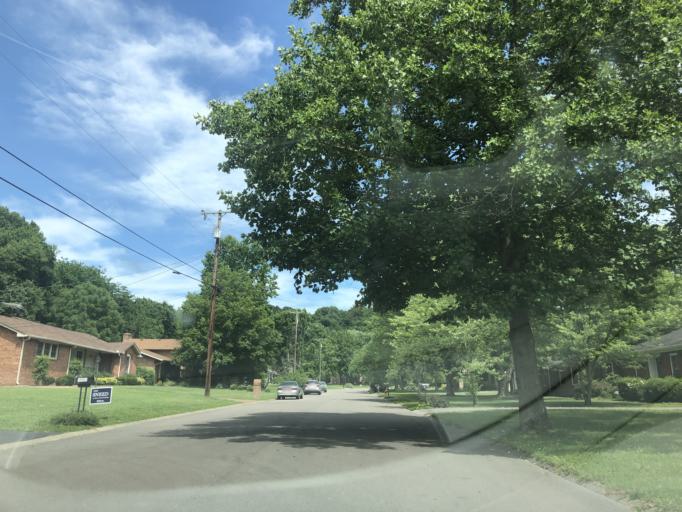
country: US
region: Tennessee
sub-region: Davidson County
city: Belle Meade
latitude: 36.0802
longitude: -86.9393
